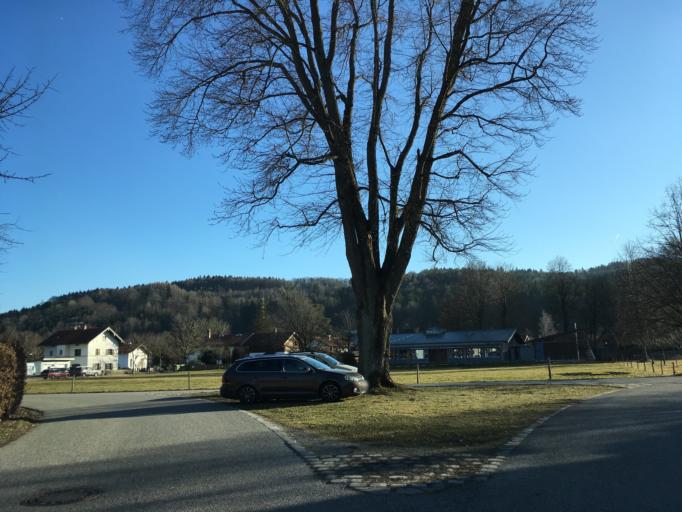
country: DE
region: Bavaria
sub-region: Upper Bavaria
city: Vagen
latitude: 47.8731
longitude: 11.8836
